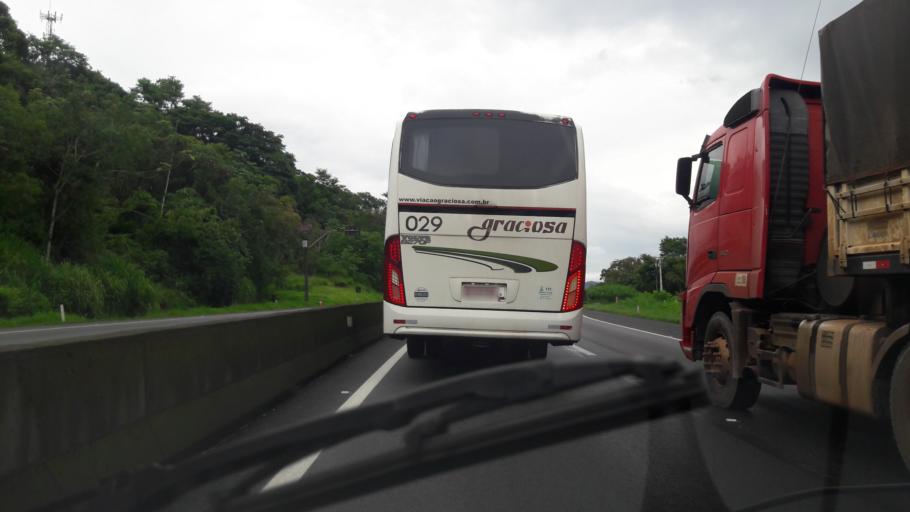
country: BR
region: Parana
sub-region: Antonina
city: Antonina
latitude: -25.5720
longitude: -48.8342
